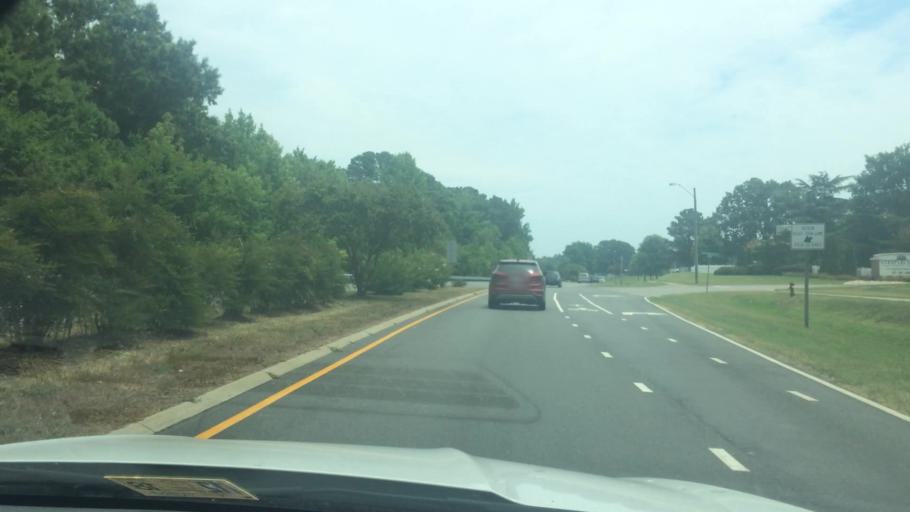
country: US
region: Virginia
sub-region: James City County
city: Williamsburg
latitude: 37.2676
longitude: -76.7644
